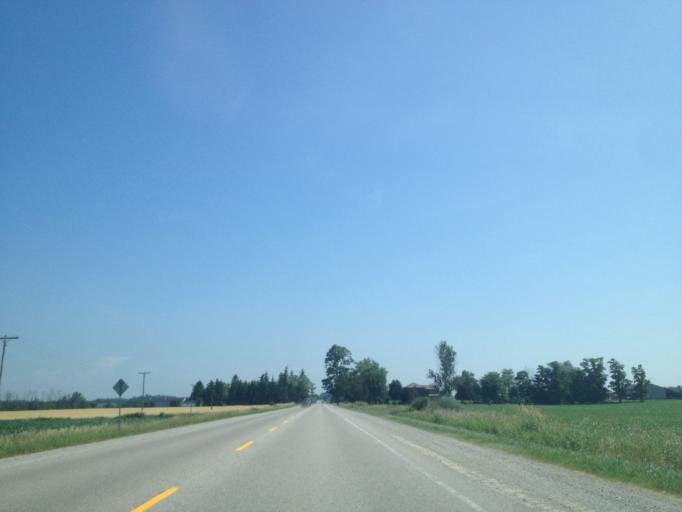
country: CA
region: Ontario
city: London
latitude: 43.2398
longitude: -81.2207
